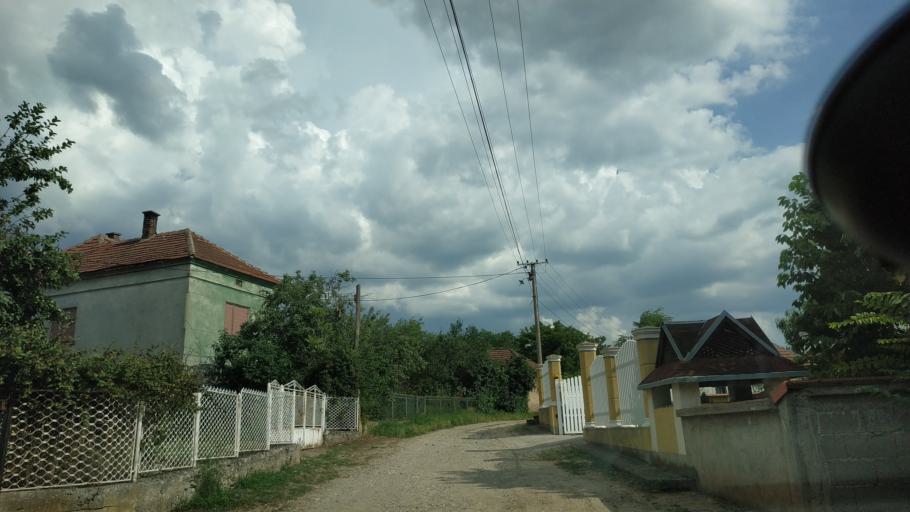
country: RS
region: Central Serbia
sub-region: Nisavski Okrug
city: Aleksinac
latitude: 43.6011
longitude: 21.6903
